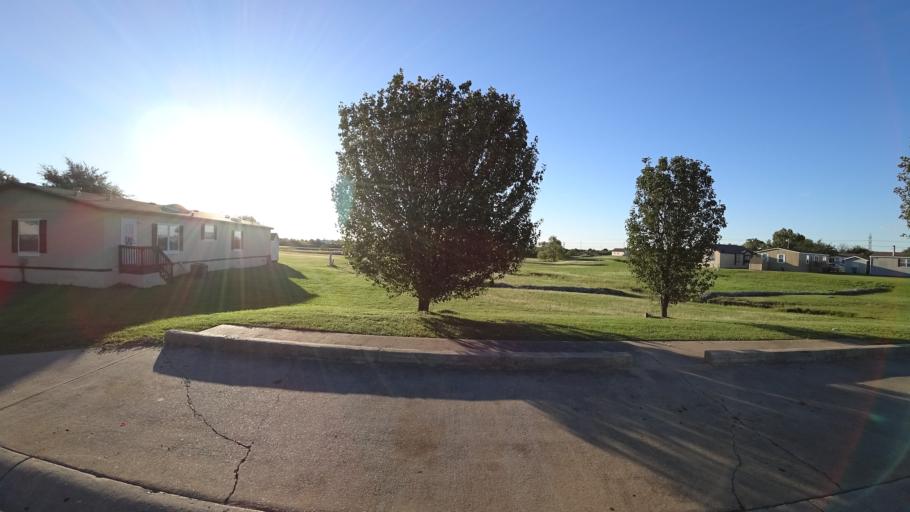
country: US
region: Texas
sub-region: Travis County
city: Manor
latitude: 30.3147
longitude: -97.6264
